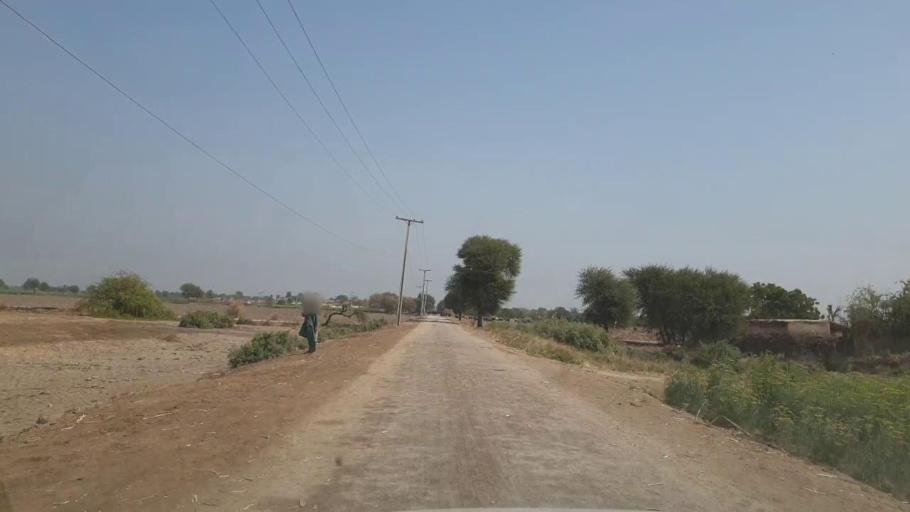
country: PK
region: Sindh
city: Mirpur Khas
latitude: 25.6633
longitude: 69.1722
